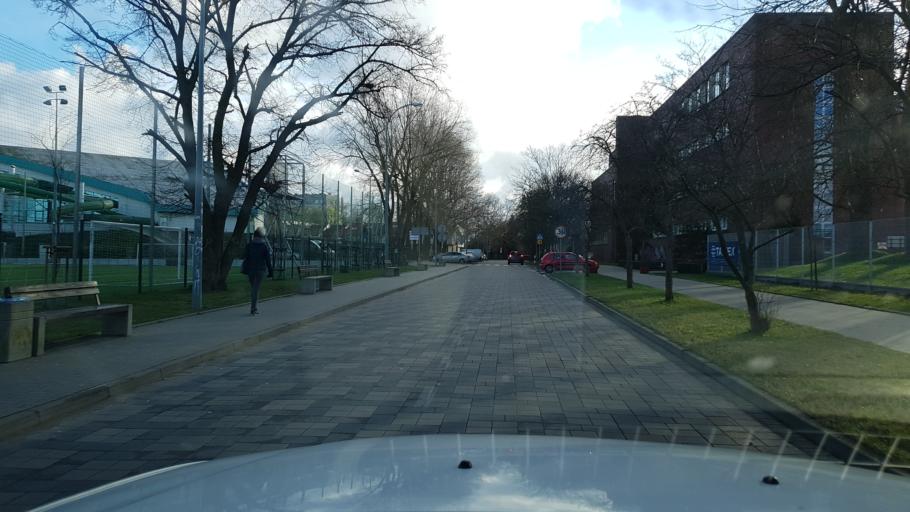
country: PL
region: West Pomeranian Voivodeship
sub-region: Powiat kolobrzeski
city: Kolobrzeg
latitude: 54.1747
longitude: 15.5629
